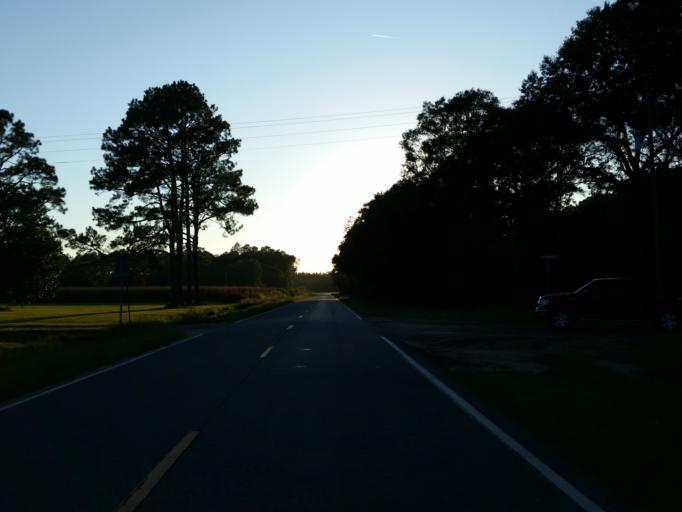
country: US
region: Georgia
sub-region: Berrien County
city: Nashville
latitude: 31.1789
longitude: -83.1311
